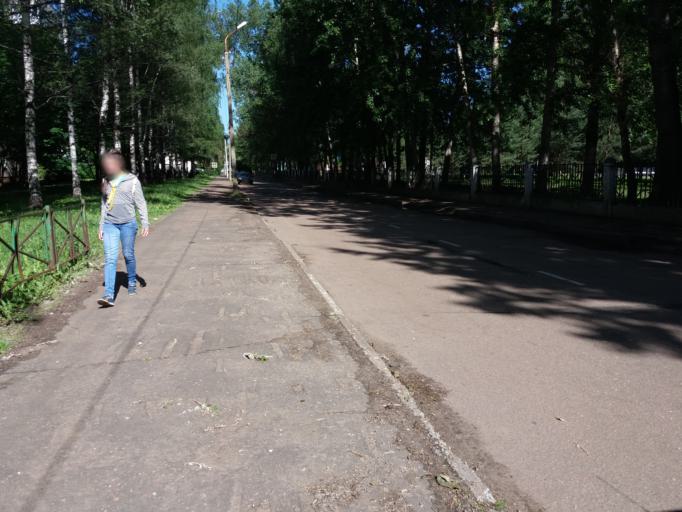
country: RU
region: Jaroslavl
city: Yaroslavl
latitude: 57.6348
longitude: 39.8561
